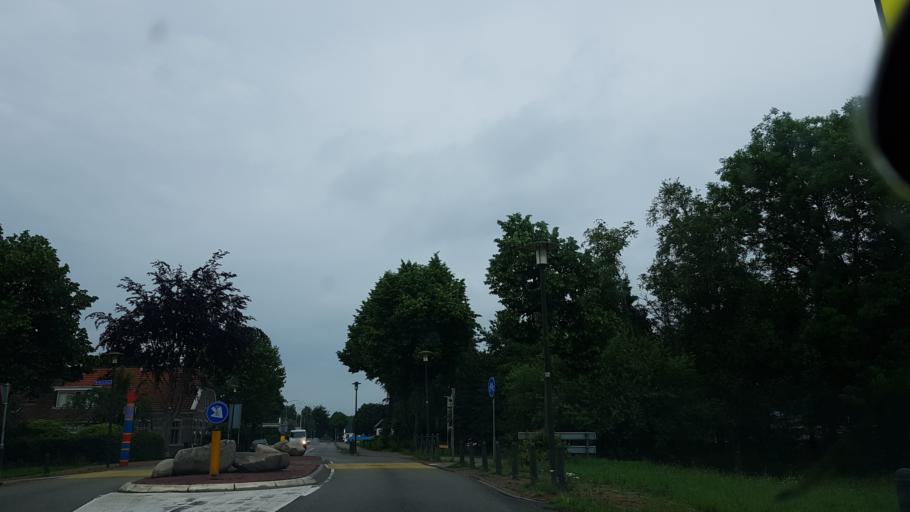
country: NL
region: Groningen
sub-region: Gemeente Hoogezand-Sappemeer
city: Hoogezand
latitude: 53.1462
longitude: 6.7238
